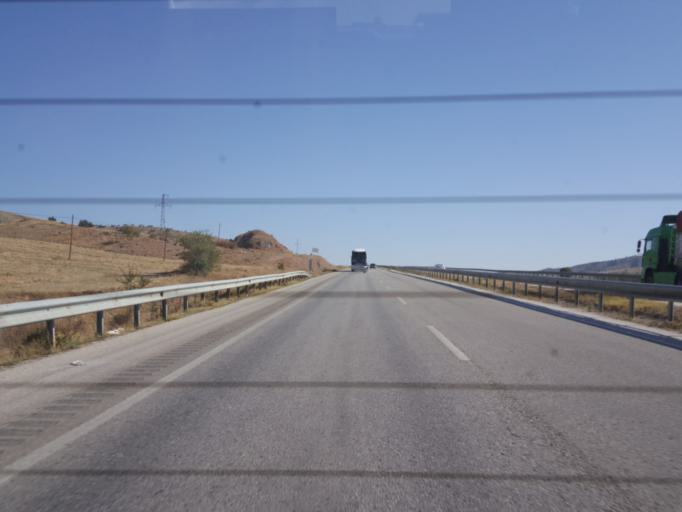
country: TR
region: Corum
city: Sungurlu
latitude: 40.2255
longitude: 34.5677
